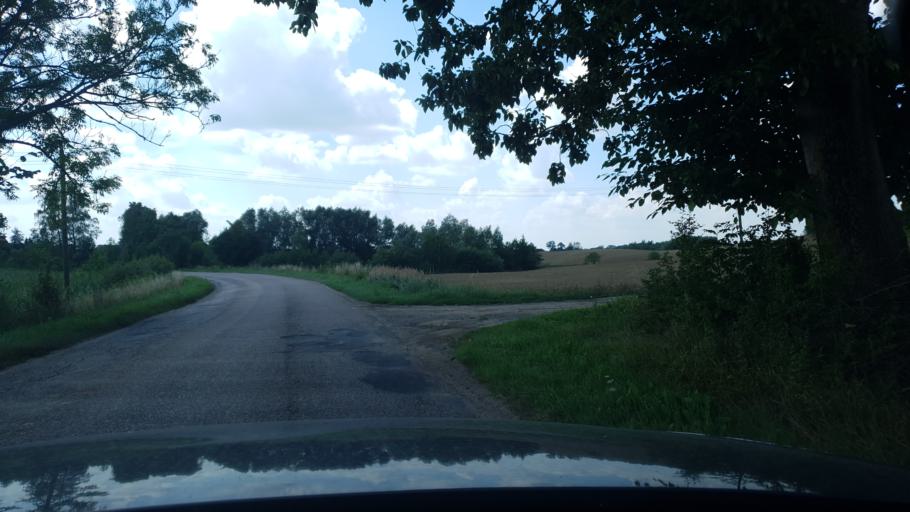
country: PL
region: Kujawsko-Pomorskie
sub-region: Powiat wabrzeski
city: Pluznica
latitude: 53.2795
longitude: 18.8334
